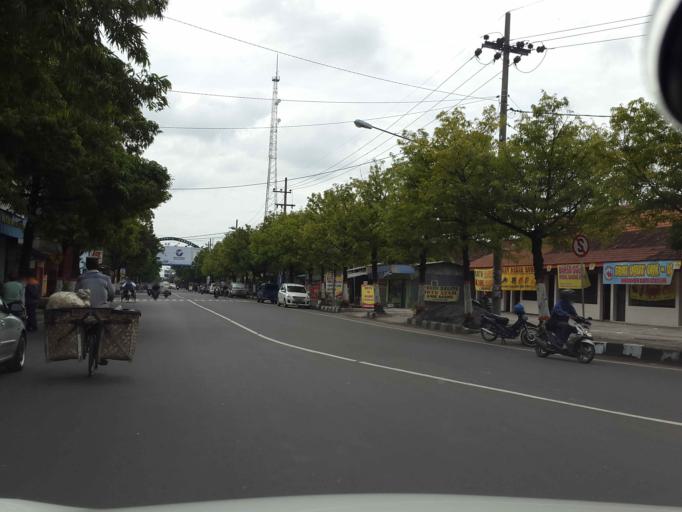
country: ID
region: East Java
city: Mojokerto
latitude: -7.4718
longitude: 112.4320
